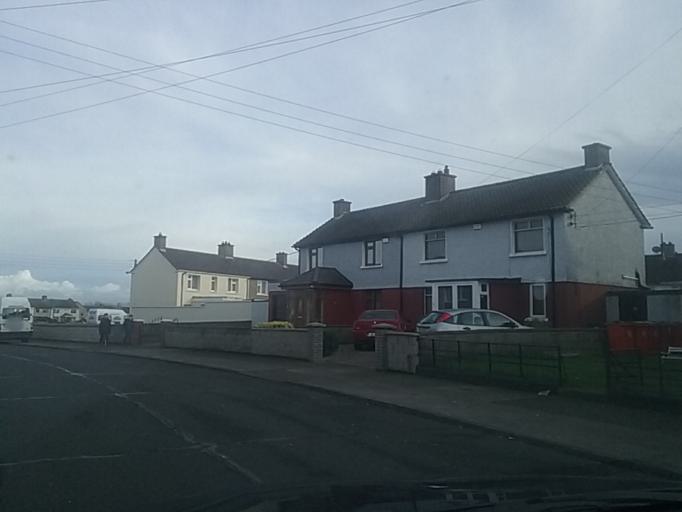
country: IE
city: Coolock
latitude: 53.3821
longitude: -6.1935
